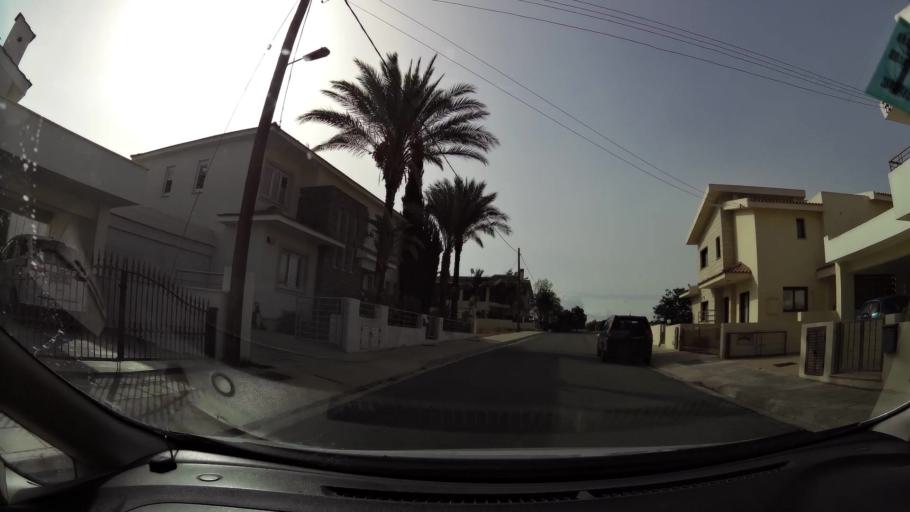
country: CY
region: Lefkosia
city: Geri
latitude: 35.0787
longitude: 33.3912
